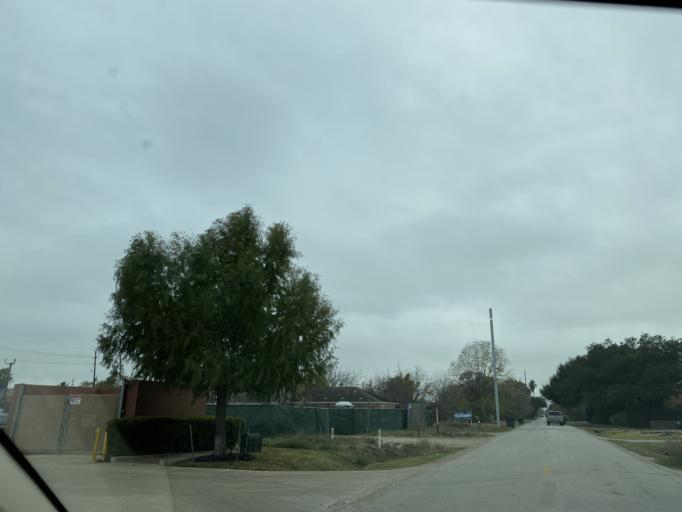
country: US
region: Texas
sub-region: Harris County
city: Bellaire
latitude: 29.7335
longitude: -95.4781
